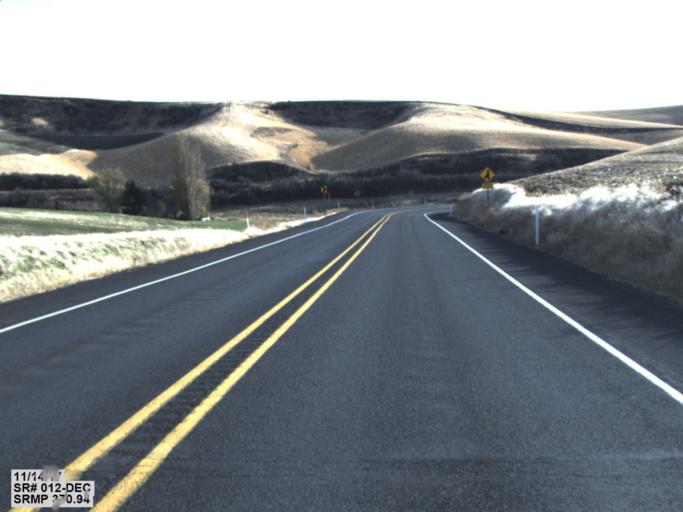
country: US
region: Washington
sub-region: Columbia County
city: Dayton
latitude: 46.3591
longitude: -117.9506
